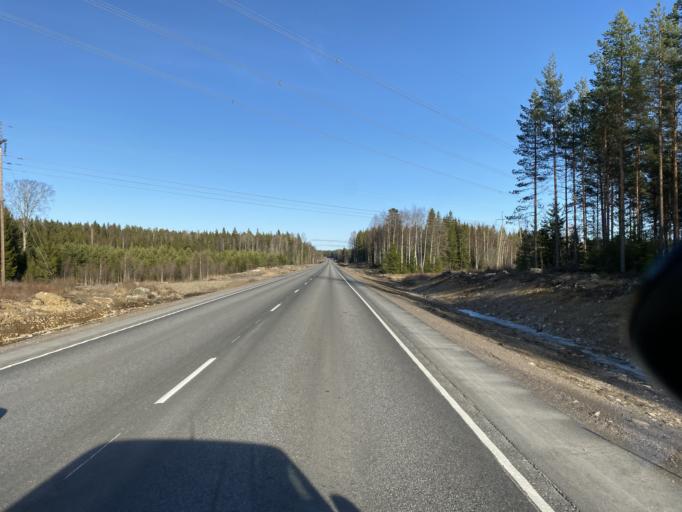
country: FI
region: Satakunta
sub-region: Pori
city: Huittinen
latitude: 61.1737
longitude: 22.5371
